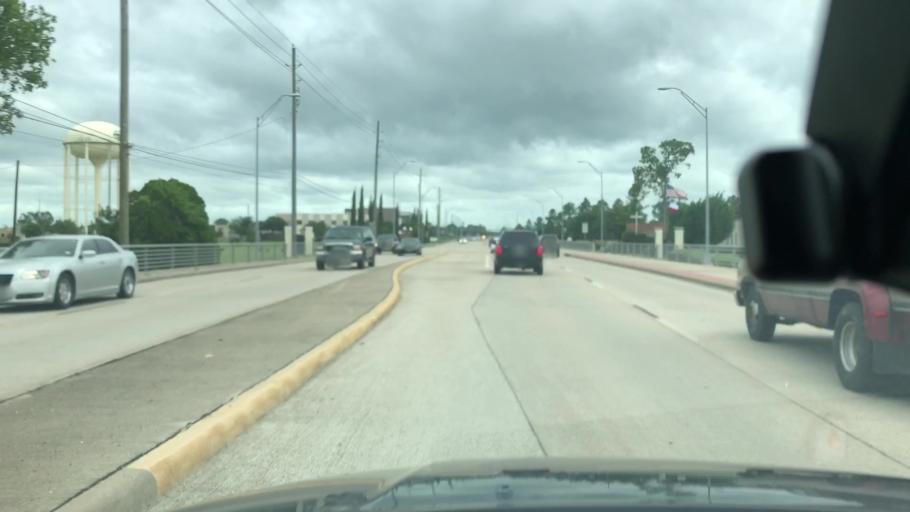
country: US
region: Texas
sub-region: Brazoria County
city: Brookside Village
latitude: 29.5659
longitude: -95.3506
